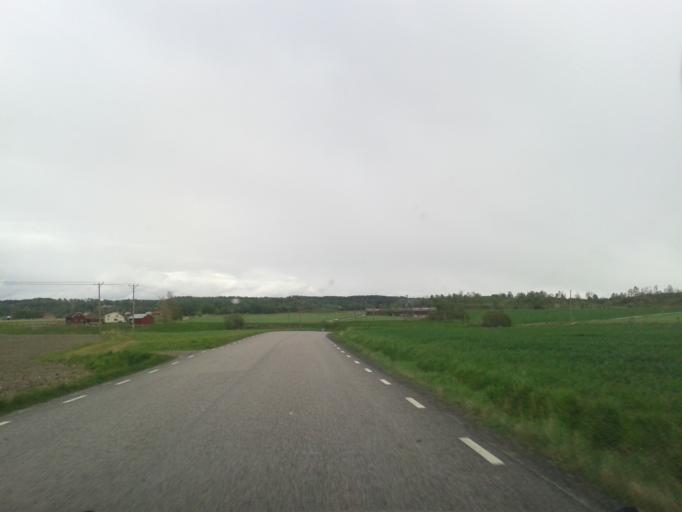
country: SE
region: Vaestra Goetaland
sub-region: Kungalvs Kommun
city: Kode
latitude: 57.9369
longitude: 11.8233
